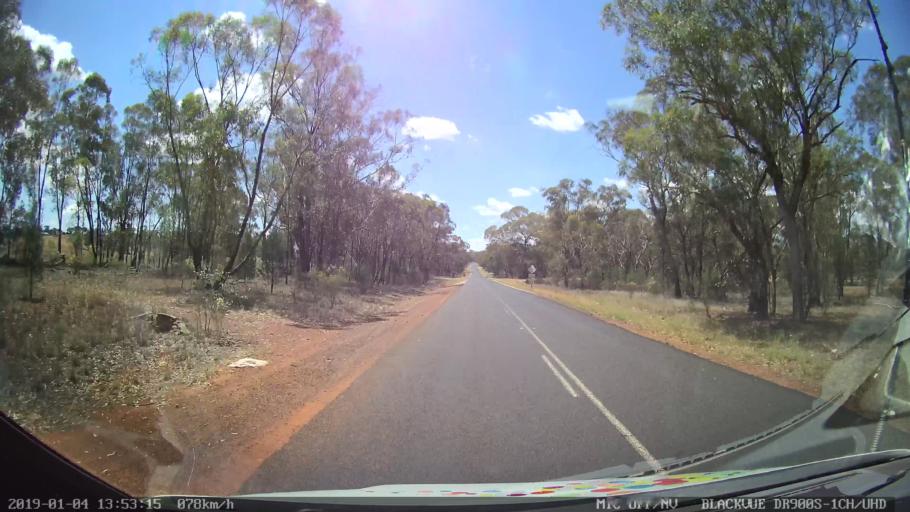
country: AU
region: New South Wales
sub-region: Dubbo Municipality
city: Dubbo
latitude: -32.3852
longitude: 148.5729
